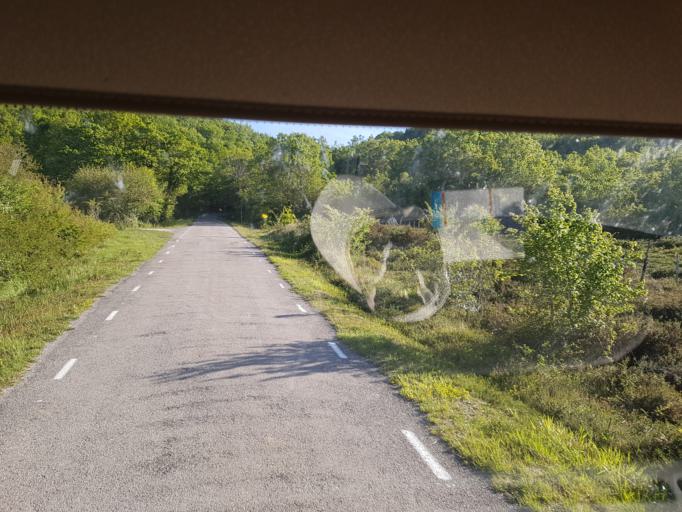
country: ES
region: Cantabria
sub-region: Provincia de Cantabria
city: San Martin de Elines
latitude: 42.9414
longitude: -3.8256
